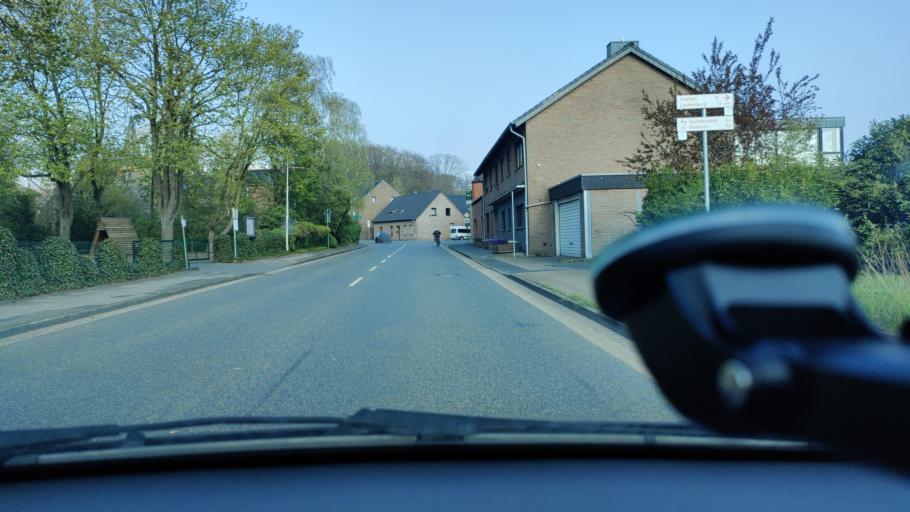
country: DE
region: North Rhine-Westphalia
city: Straelen
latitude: 51.3892
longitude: 6.2523
